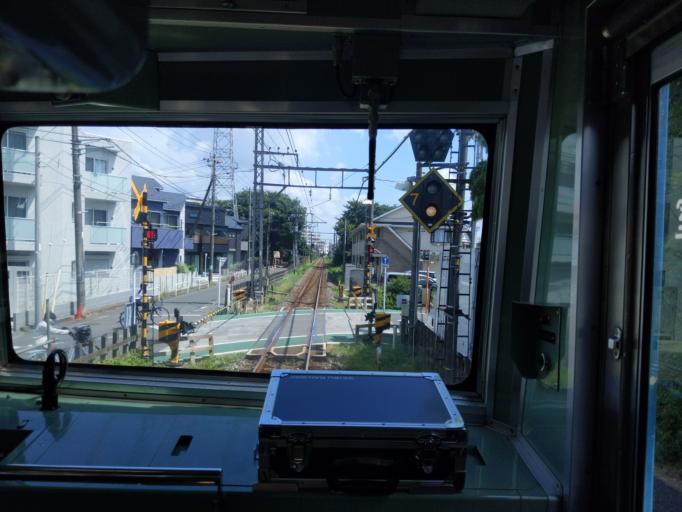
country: JP
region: Tokyo
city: Kamirenjaku
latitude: 35.6995
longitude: 139.5321
